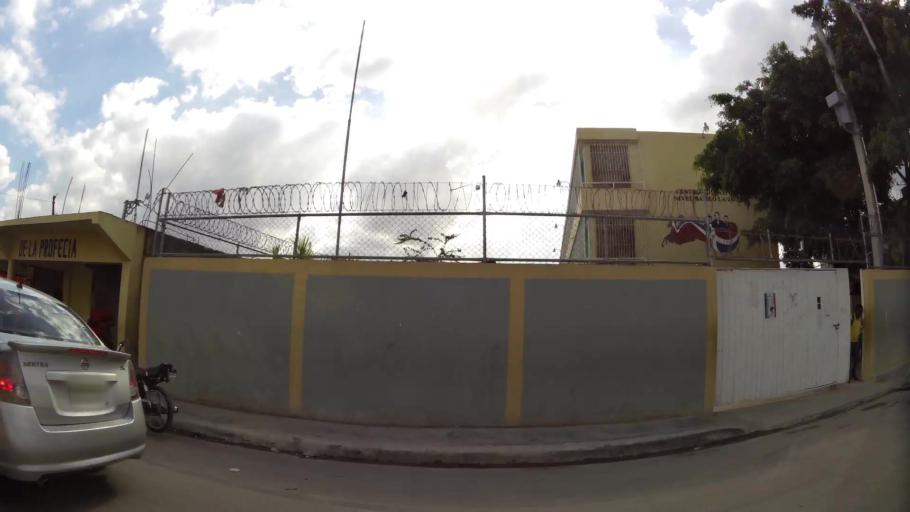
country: DO
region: Nacional
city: Ensanche Luperon
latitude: 18.5400
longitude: -69.8848
